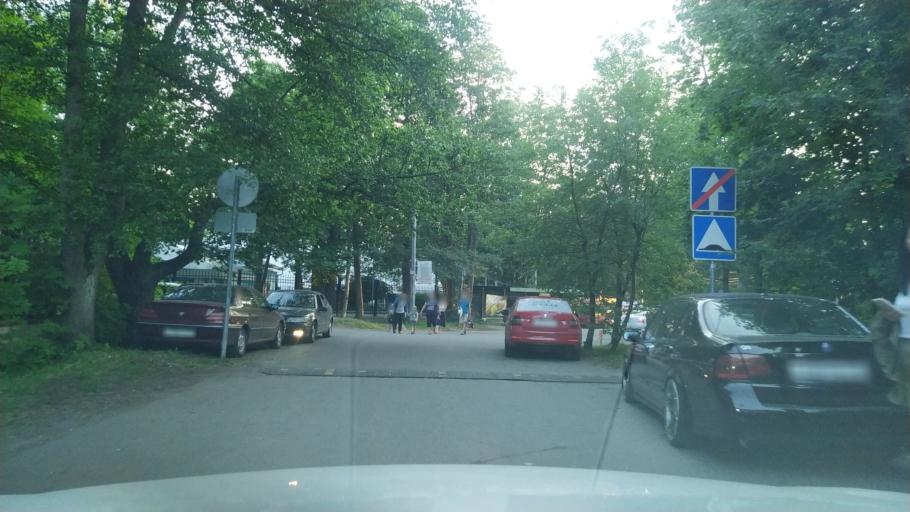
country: RU
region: St.-Petersburg
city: Sestroretsk
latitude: 60.0926
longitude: 29.9427
